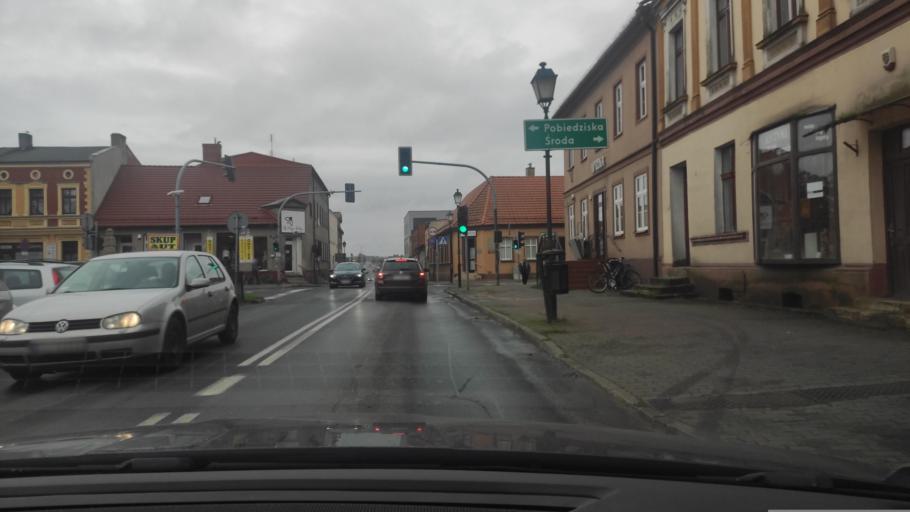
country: PL
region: Greater Poland Voivodeship
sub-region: Powiat poznanski
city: Kostrzyn
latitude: 52.3980
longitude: 17.2274
